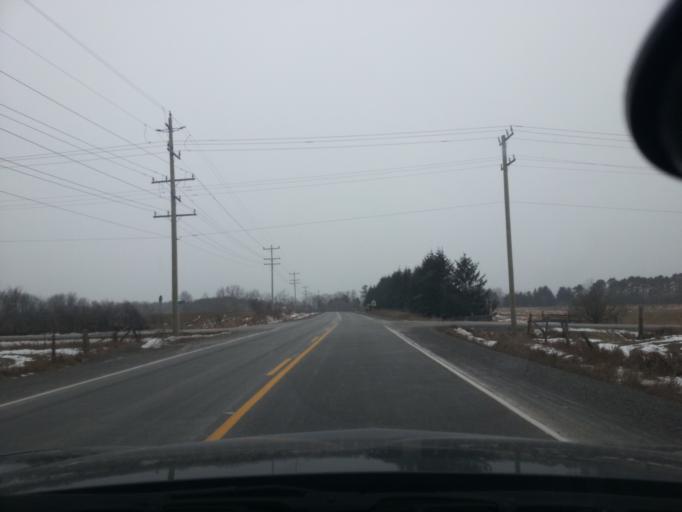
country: CA
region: Ontario
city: Arnprior
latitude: 45.3353
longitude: -76.2784
